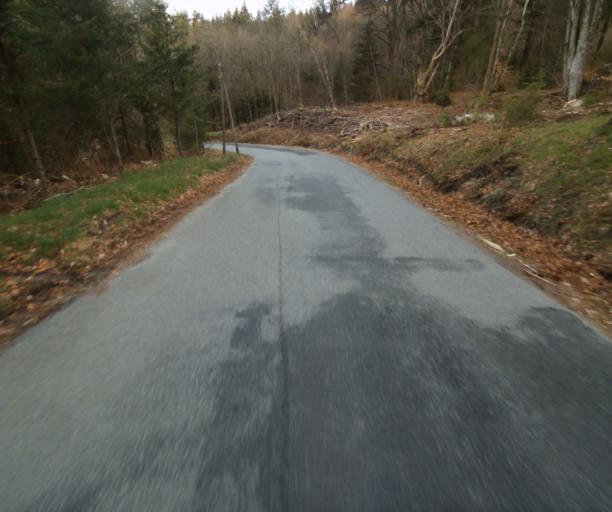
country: FR
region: Limousin
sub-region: Departement de la Correze
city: Correze
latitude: 45.4199
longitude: 1.8873
